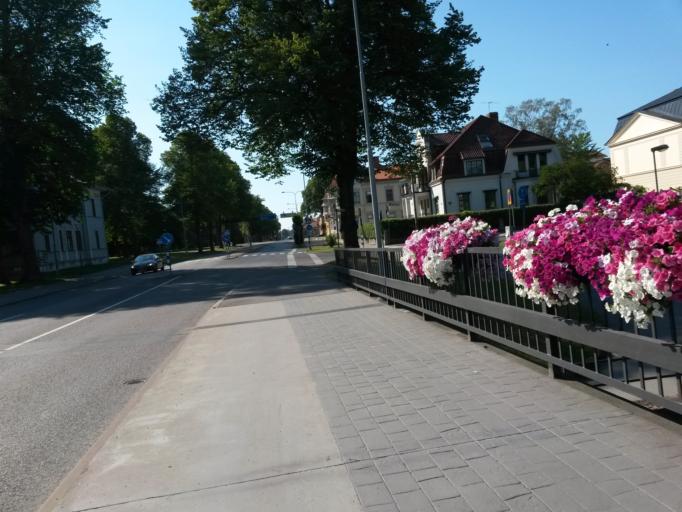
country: SE
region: Vaestra Goetaland
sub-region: Lidkopings Kommun
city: Lidkoping
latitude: 58.5008
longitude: 13.1571
